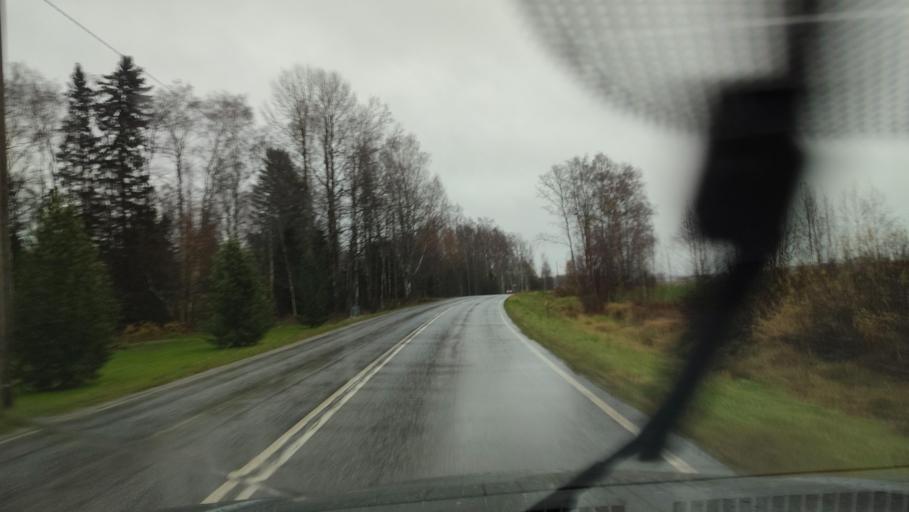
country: FI
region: Ostrobothnia
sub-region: Vaasa
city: Ristinummi
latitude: 63.0484
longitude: 21.7369
